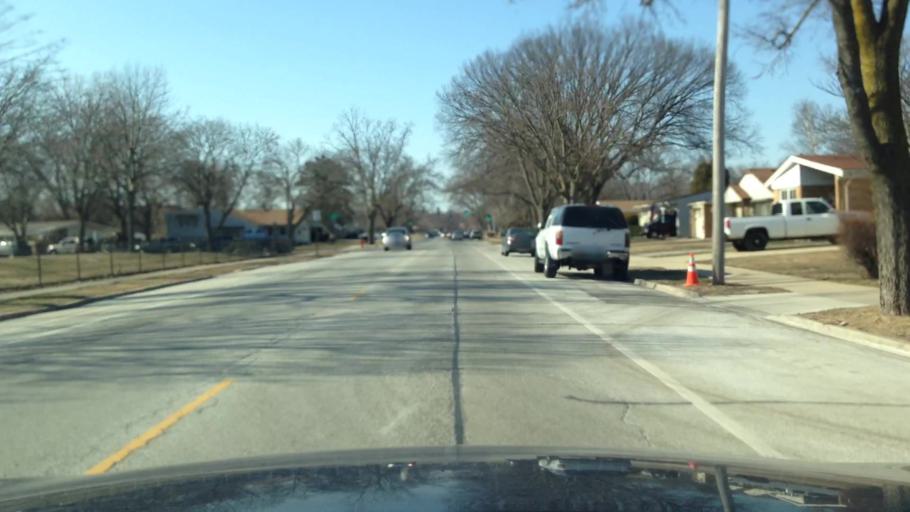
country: US
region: Illinois
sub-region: Cook County
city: Glenview
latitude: 42.0534
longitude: -87.8100
